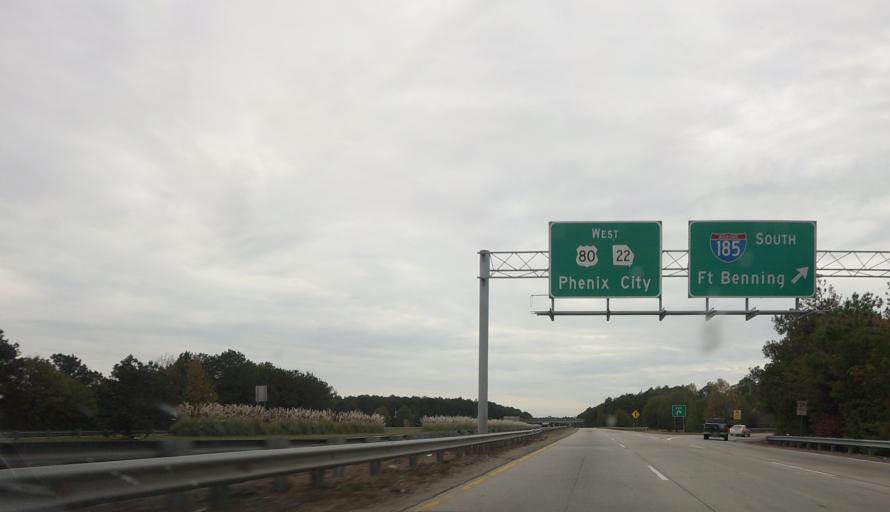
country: US
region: Alabama
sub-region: Russell County
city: Phenix City
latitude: 32.5449
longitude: -84.9619
